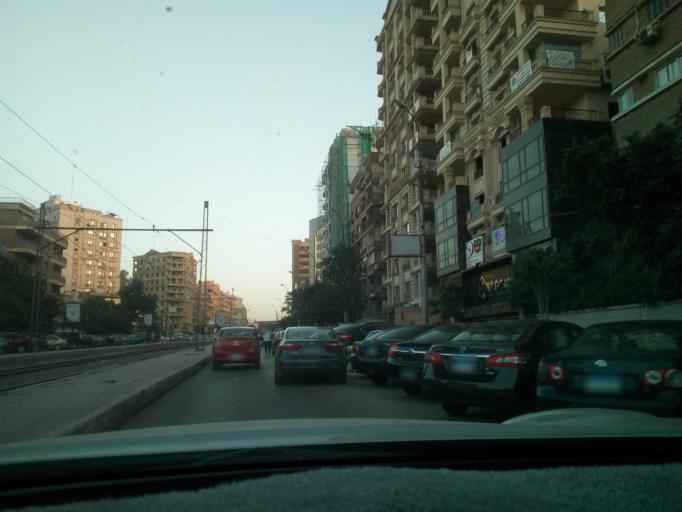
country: EG
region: Muhafazat al Qahirah
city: Cairo
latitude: 30.0888
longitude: 31.3442
